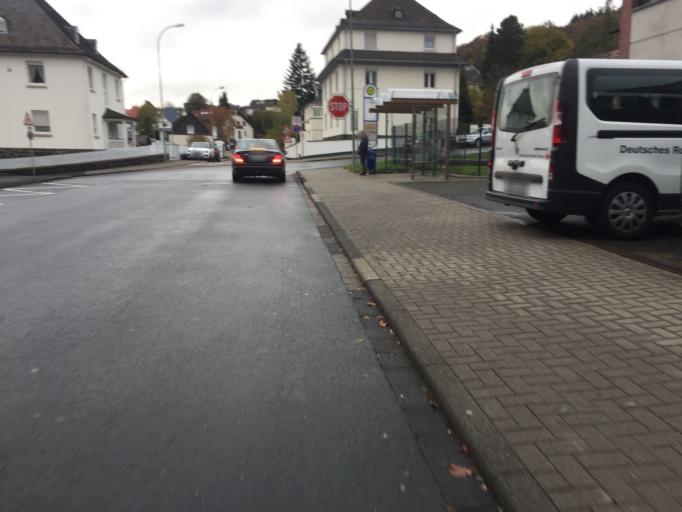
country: DE
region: Hesse
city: Dillenburg
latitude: 50.7443
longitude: 8.2844
